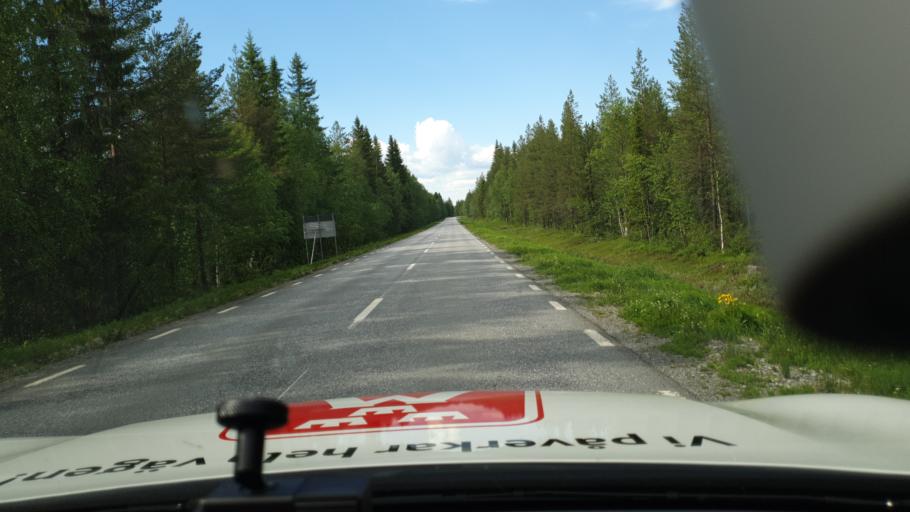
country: SE
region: Vaesterbotten
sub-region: Storumans Kommun
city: Storuman
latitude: 65.1193
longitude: 17.1159
